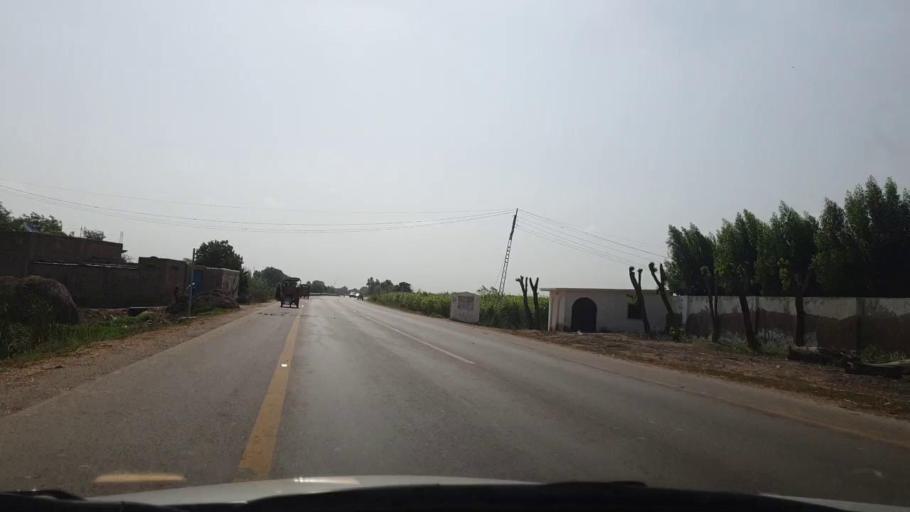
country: PK
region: Sindh
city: Matli
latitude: 25.0729
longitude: 68.6205
